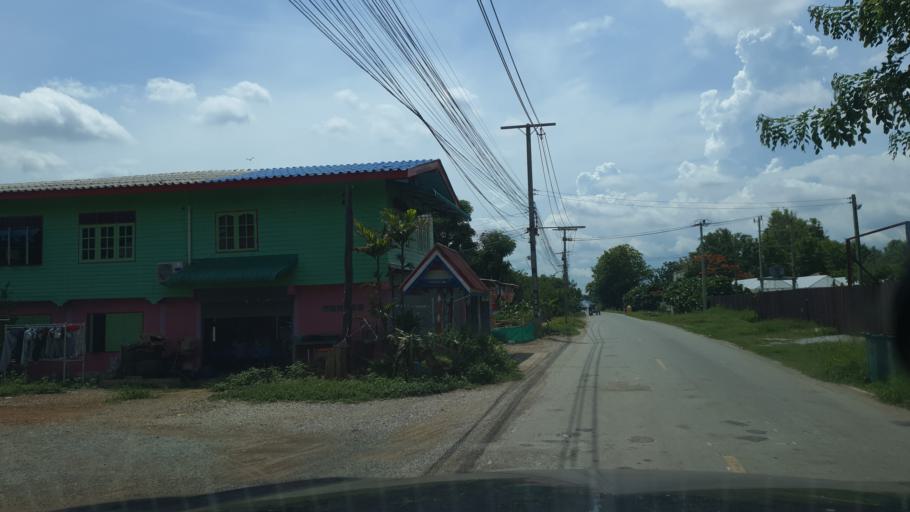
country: TH
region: Sukhothai
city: Sukhothai
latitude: 16.9963
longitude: 99.8562
